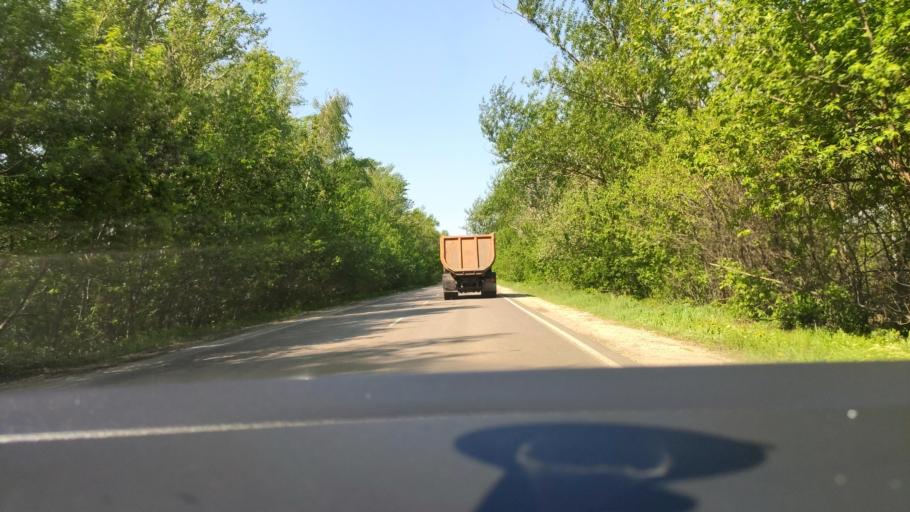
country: RU
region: Voronezj
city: Maslovka
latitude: 51.5302
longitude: 39.2994
